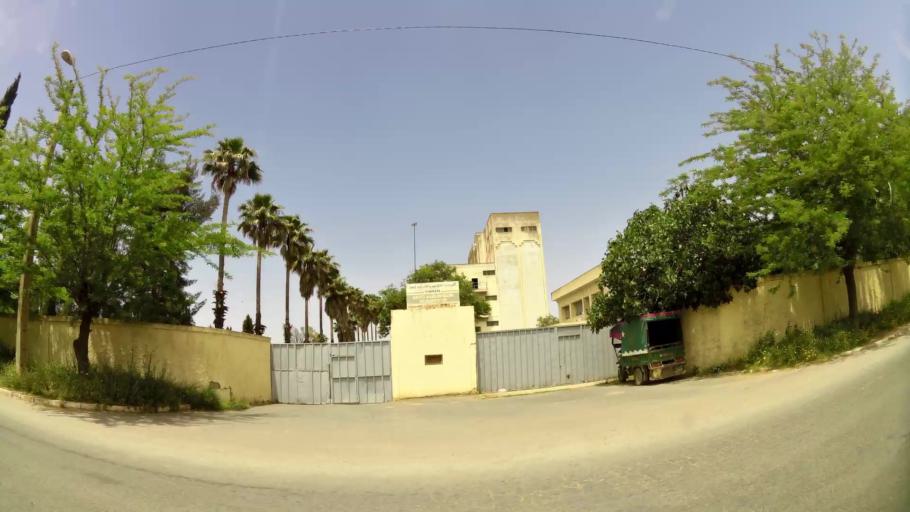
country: MA
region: Rabat-Sale-Zemmour-Zaer
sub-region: Khemisset
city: Khemisset
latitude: 33.8210
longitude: -6.0820
